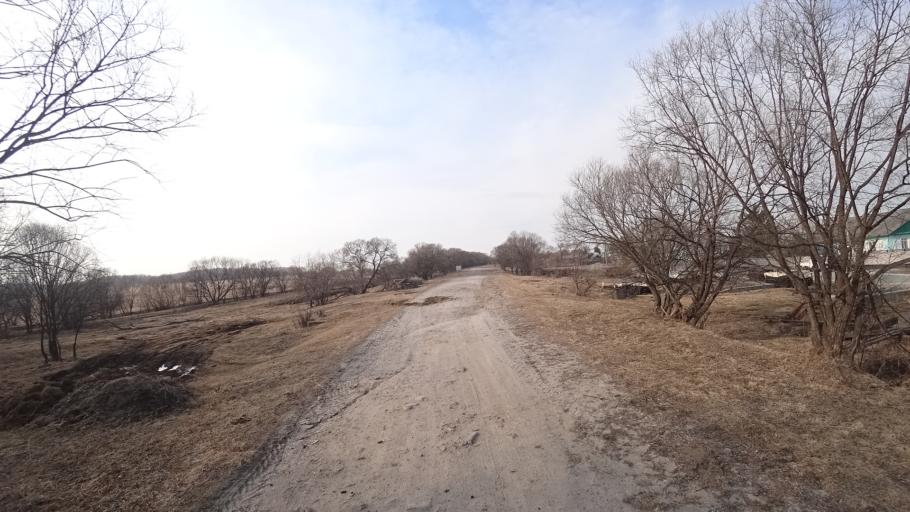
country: RU
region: Amur
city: Novobureyskiy
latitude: 49.8954
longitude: 129.8746
